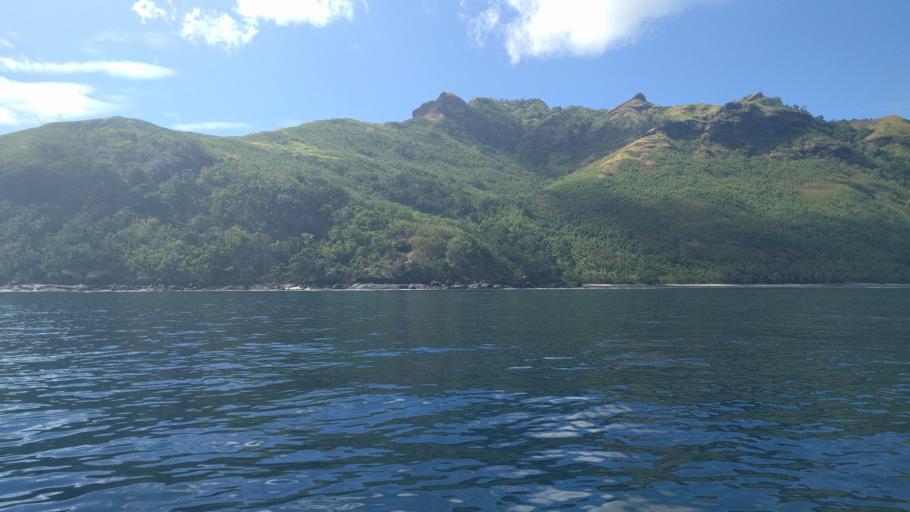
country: FJ
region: Western
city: Lautoka
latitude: -17.2916
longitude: 177.1002
